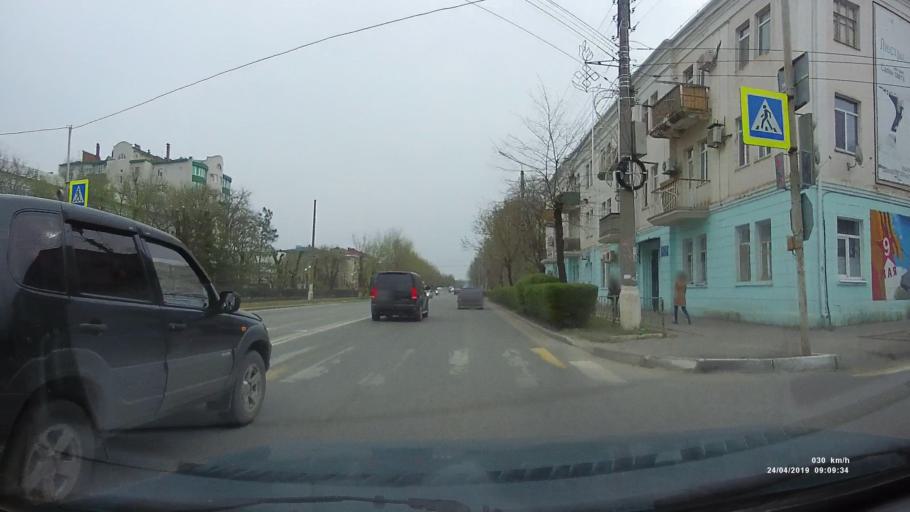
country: RU
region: Kalmykiya
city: Elista
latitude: 46.3089
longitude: 44.2718
